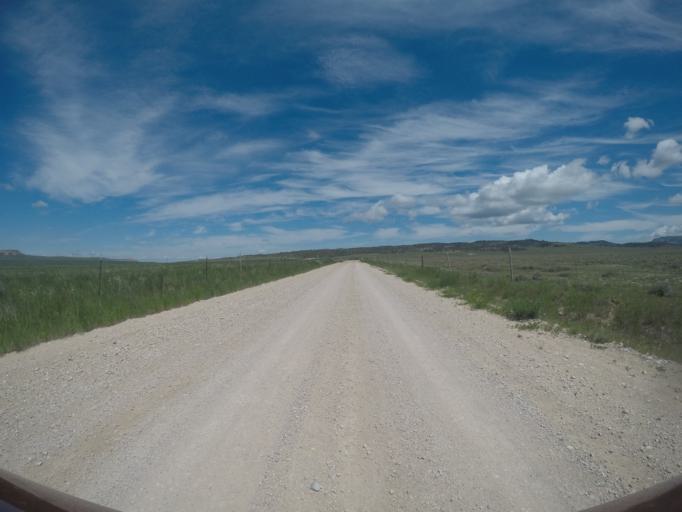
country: US
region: Montana
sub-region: Yellowstone County
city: Laurel
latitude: 45.2305
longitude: -108.6995
